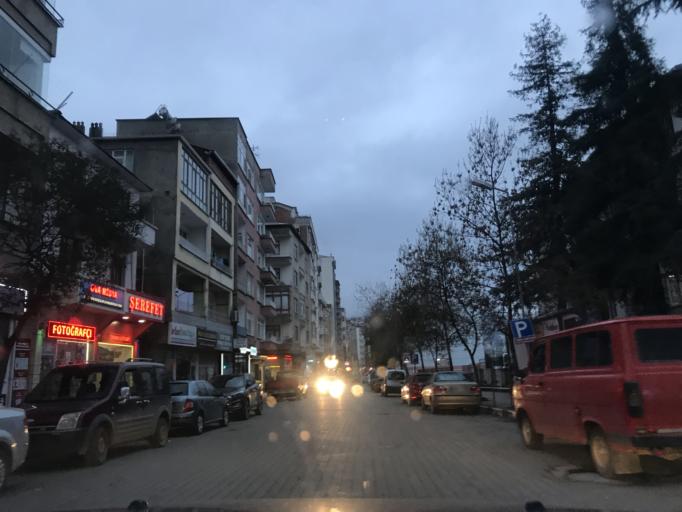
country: TR
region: Trabzon
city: Akcaabat
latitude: 41.0210
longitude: 39.5759
